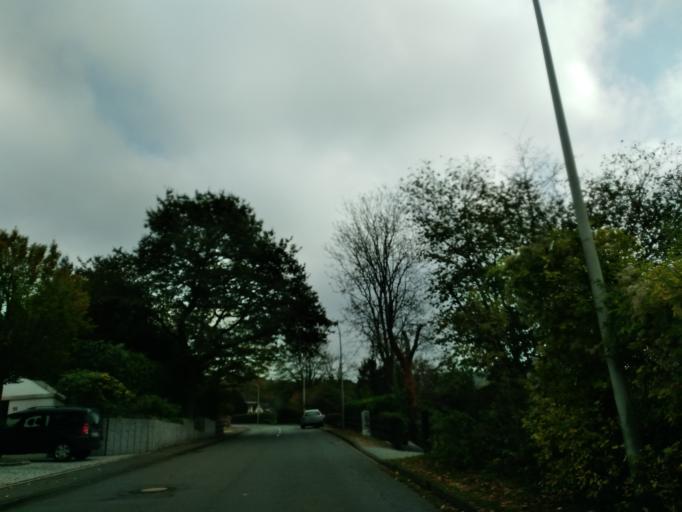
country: DE
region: North Rhine-Westphalia
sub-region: Regierungsbezirk Koln
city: Konigswinter
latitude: 50.7114
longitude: 7.1817
